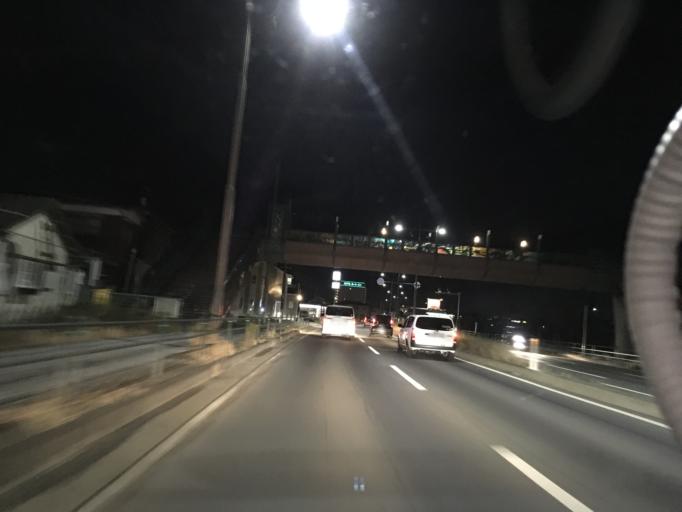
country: JP
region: Miyagi
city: Ishinomaki
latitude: 38.4426
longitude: 141.2778
